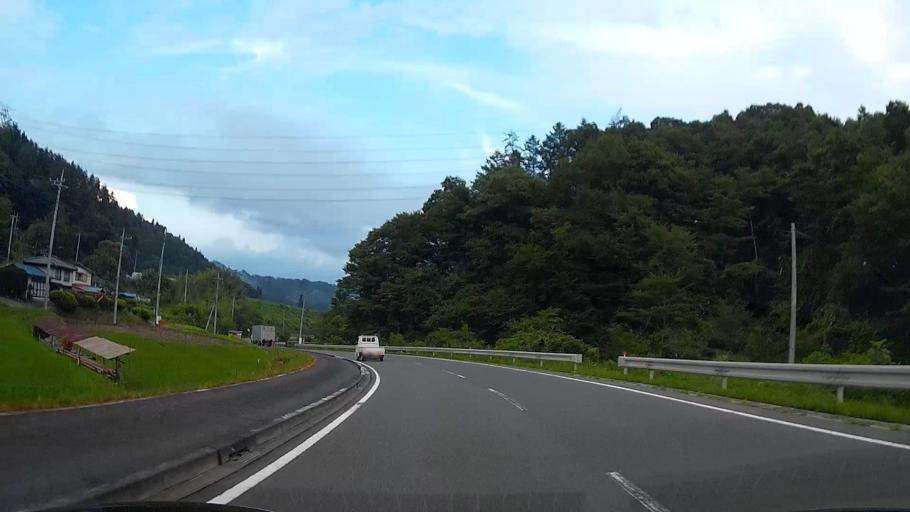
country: JP
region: Gunma
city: Nakanojomachi
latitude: 36.5271
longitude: 138.7393
